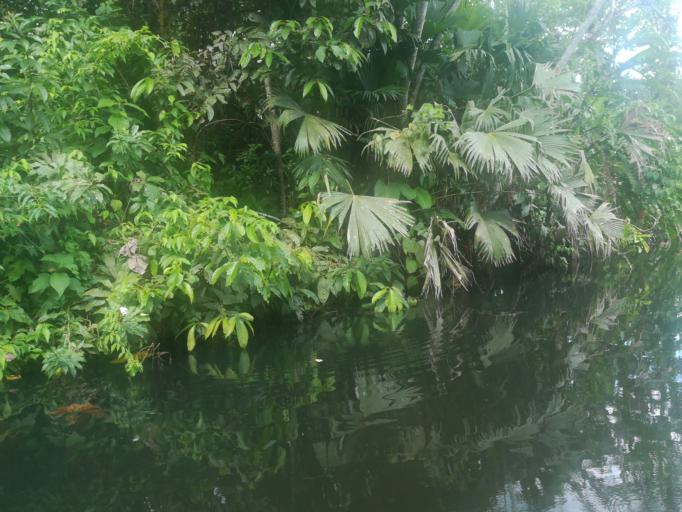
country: EC
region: Napo
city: Tena
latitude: -1.0392
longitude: -77.6648
